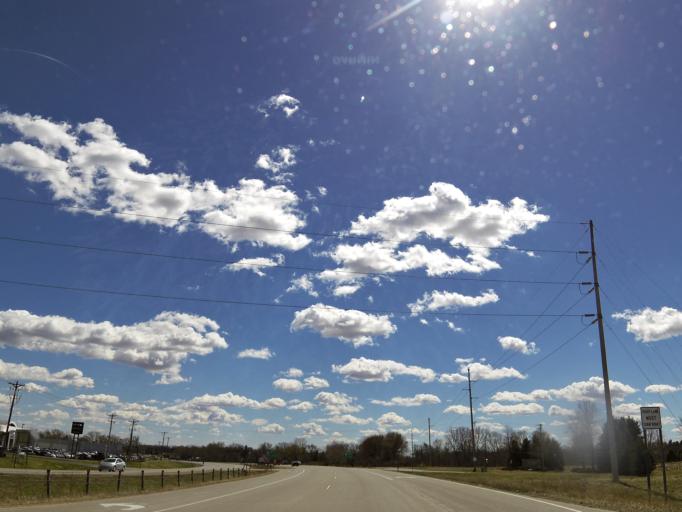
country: US
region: Minnesota
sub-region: Dakota County
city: Hastings
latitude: 44.7717
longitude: -92.8633
